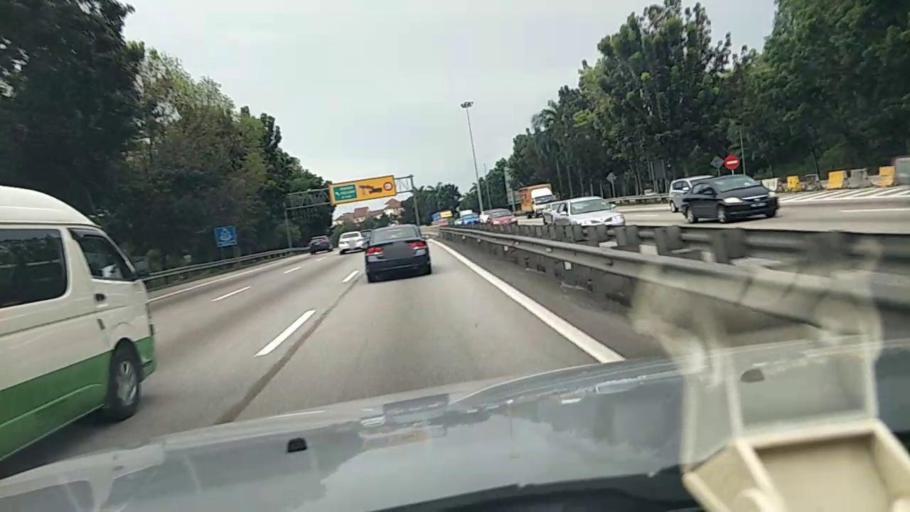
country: MY
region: Selangor
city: Subang Jaya
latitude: 3.0609
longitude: 101.5580
